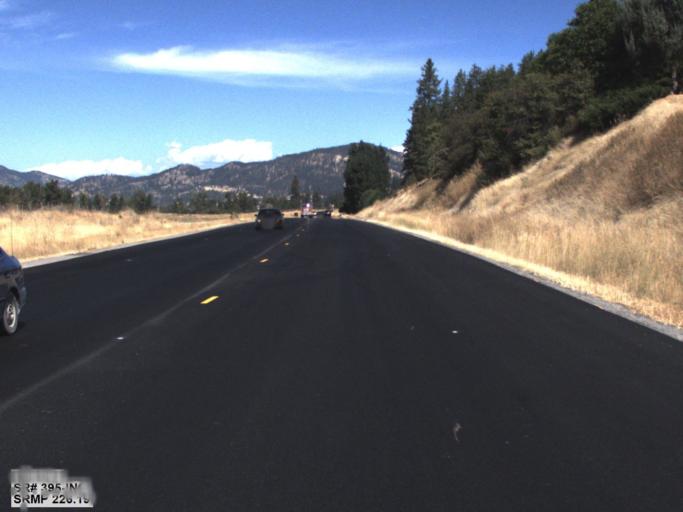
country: US
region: Washington
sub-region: Stevens County
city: Colville
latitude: 48.4969
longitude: -117.9022
